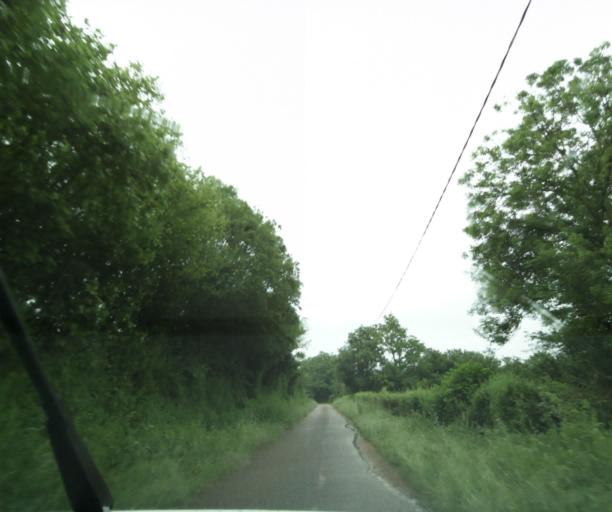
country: FR
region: Bourgogne
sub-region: Departement de Saone-et-Loire
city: Charolles
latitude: 46.3902
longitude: 4.3358
